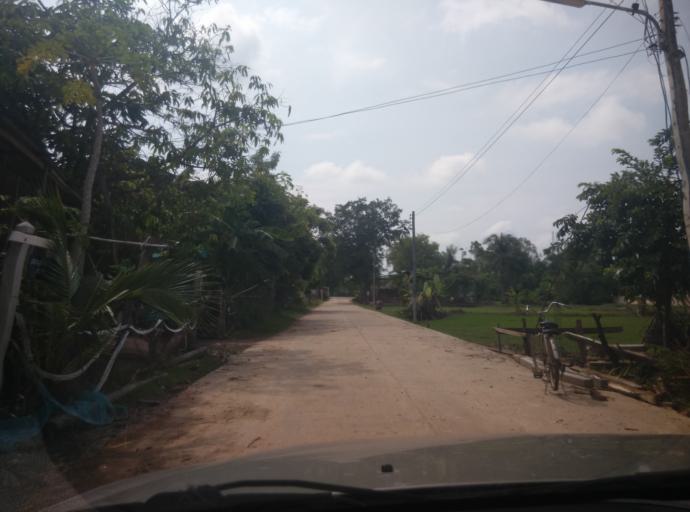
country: TH
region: Sisaket
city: Huai Thap Than
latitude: 15.0268
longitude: 104.0725
